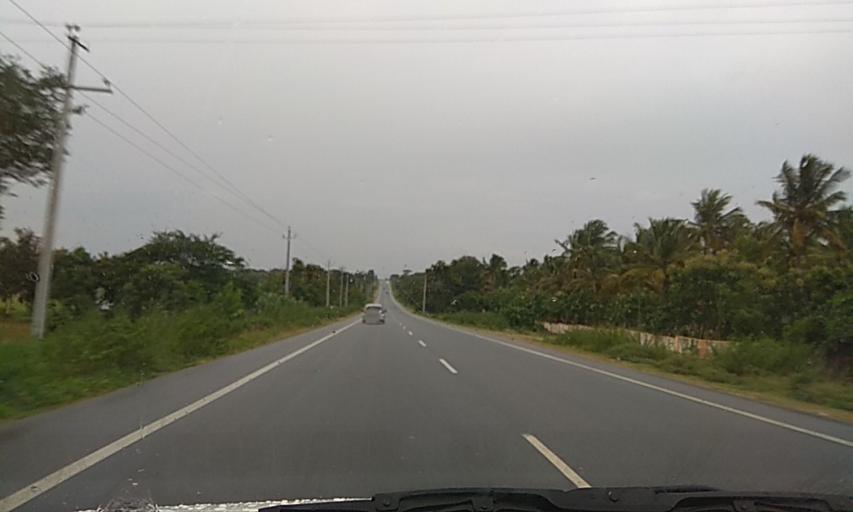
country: IN
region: Karnataka
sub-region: Chamrajnagar
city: Gundlupet
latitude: 11.9540
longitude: 76.6706
